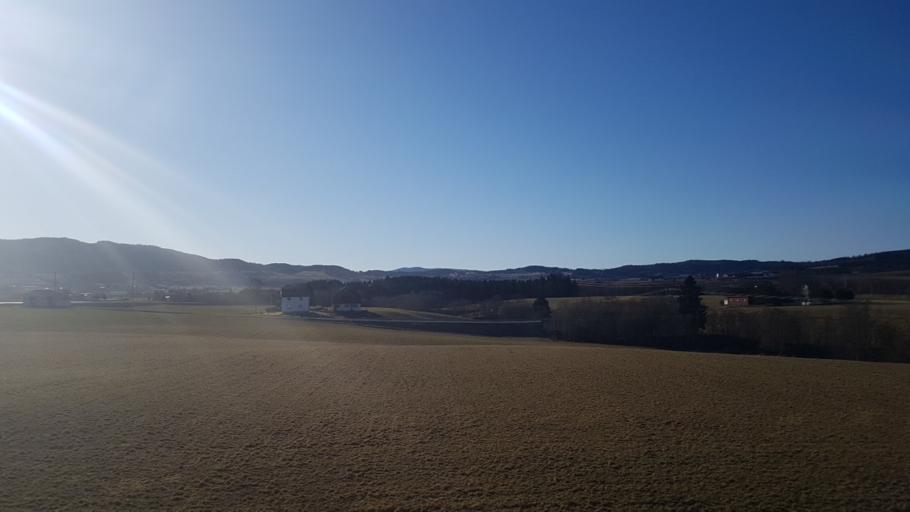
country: NO
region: Nord-Trondelag
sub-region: Levanger
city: Skogn
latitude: 63.6968
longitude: 11.1823
